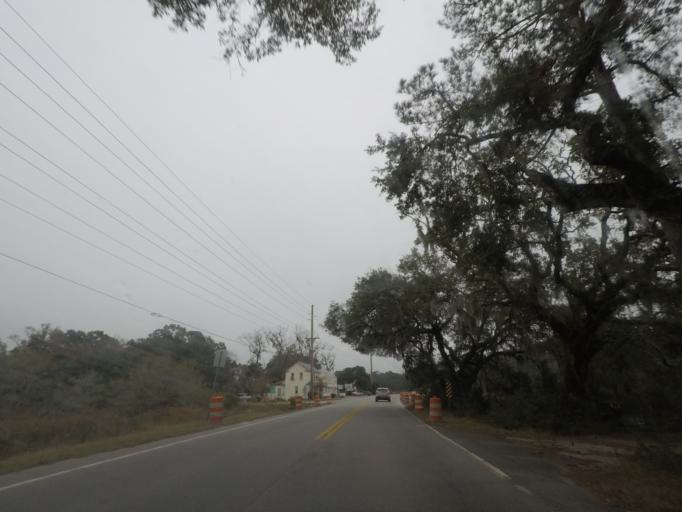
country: US
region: South Carolina
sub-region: Charleston County
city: Seabrook Island
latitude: 32.5609
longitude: -80.2801
